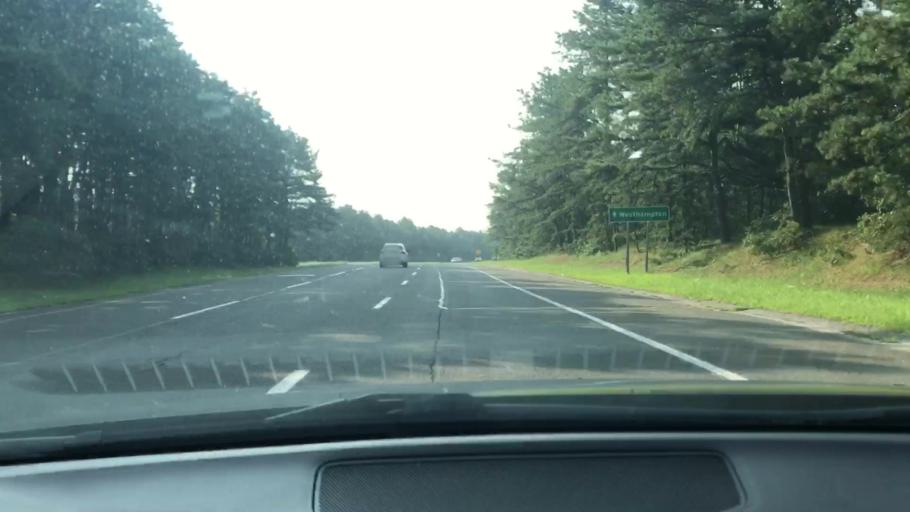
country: US
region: New York
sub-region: Suffolk County
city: Riverhead
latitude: 40.8977
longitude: -72.6498
